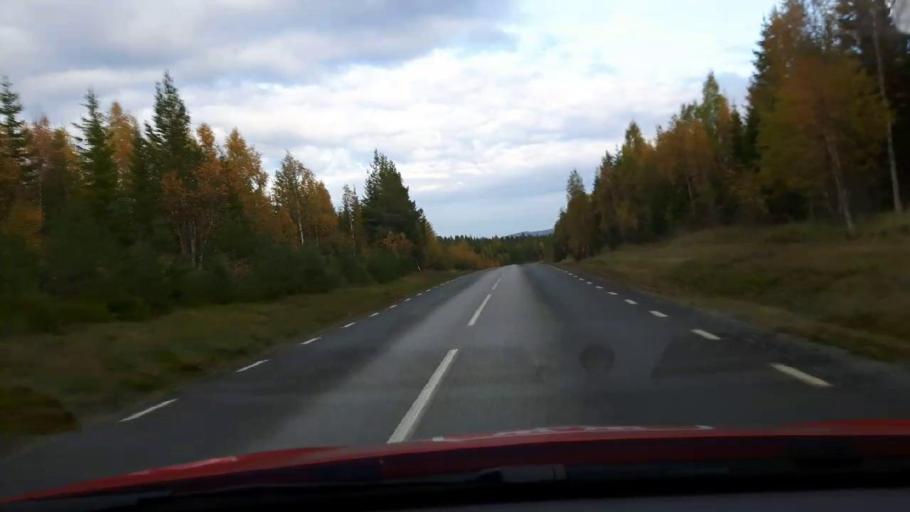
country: SE
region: Jaemtland
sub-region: OEstersunds Kommun
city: Ostersund
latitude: 63.3265
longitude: 14.6194
